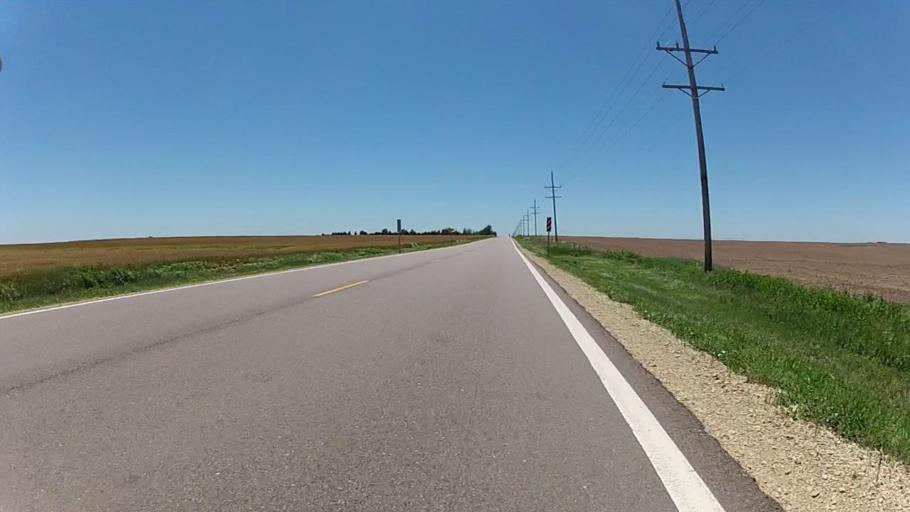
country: US
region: Kansas
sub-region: Kiowa County
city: Greensburg
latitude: 37.5235
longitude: -99.3207
